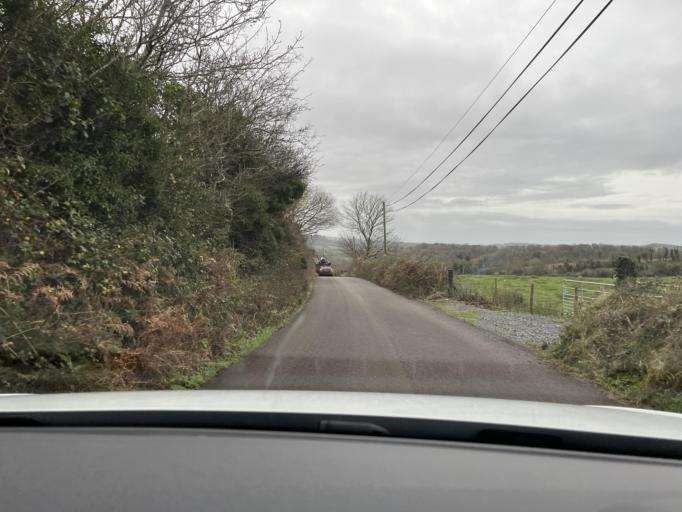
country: IE
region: Connaught
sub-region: County Leitrim
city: Manorhamilton
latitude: 54.2346
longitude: -8.2828
